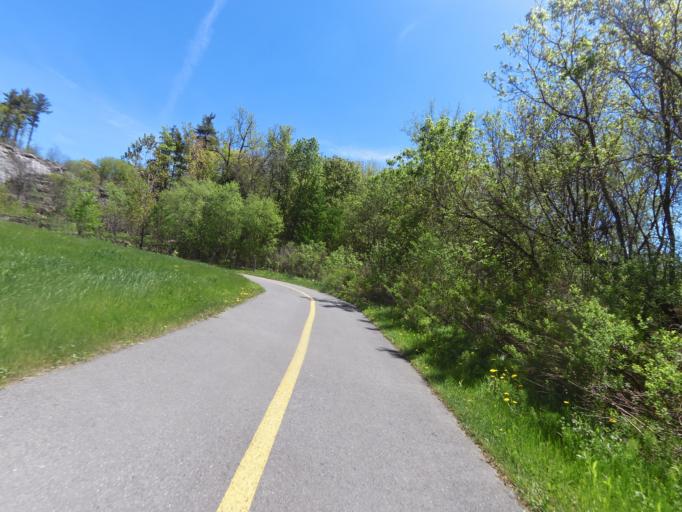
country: CA
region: Ontario
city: Ottawa
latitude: 45.4333
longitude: -75.7546
